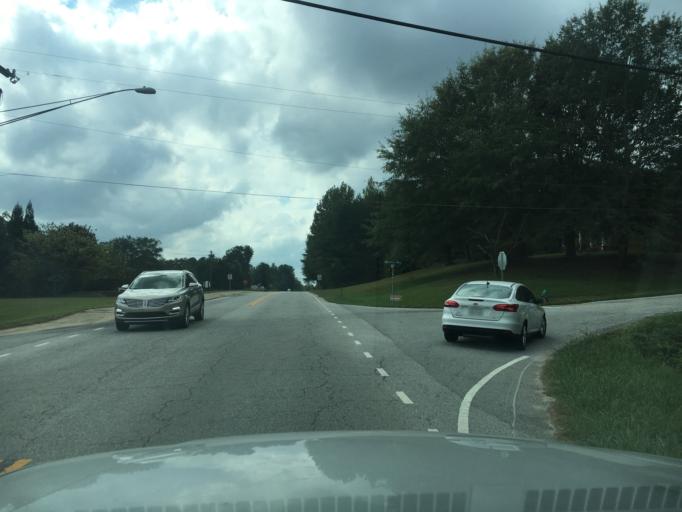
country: US
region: South Carolina
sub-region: Spartanburg County
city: Landrum
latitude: 35.1688
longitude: -82.1960
